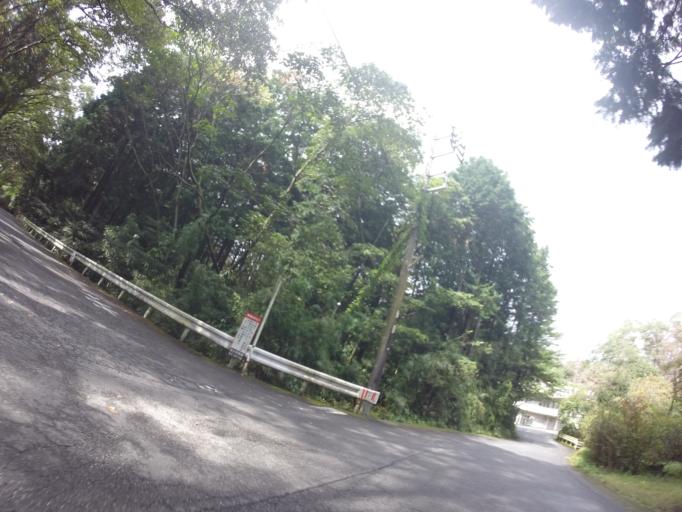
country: JP
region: Shizuoka
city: Fuji
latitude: 35.2288
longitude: 138.6847
